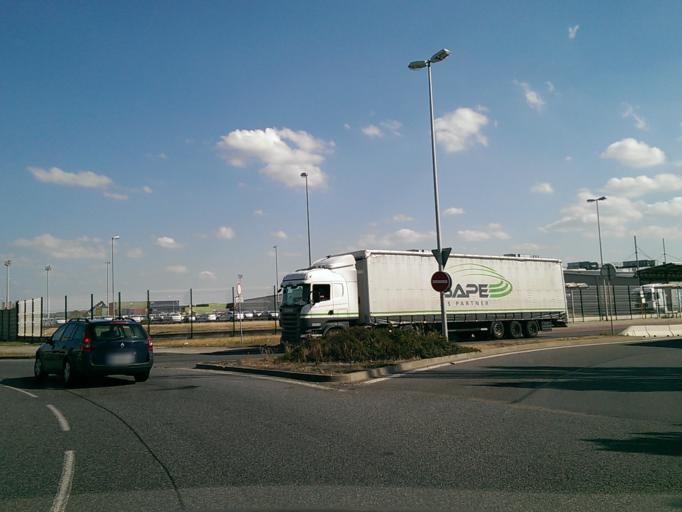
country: CZ
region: Central Bohemia
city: Kosmonosy
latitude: 50.4278
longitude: 14.9385
